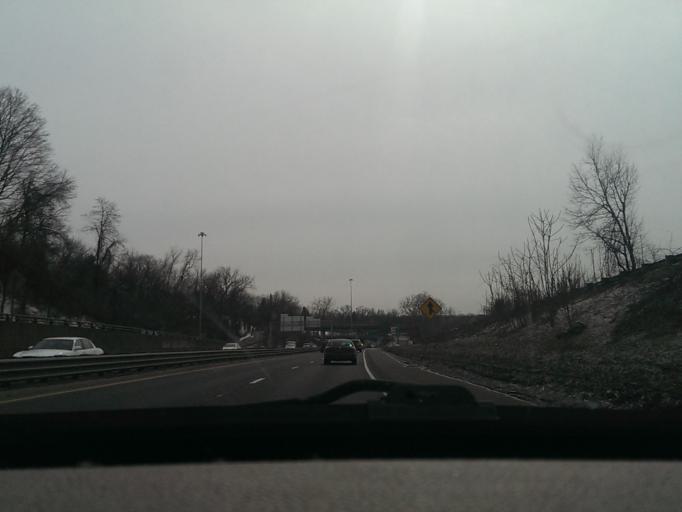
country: US
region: Massachusetts
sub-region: Hampden County
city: Springfield
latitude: 42.0815
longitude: -72.5793
